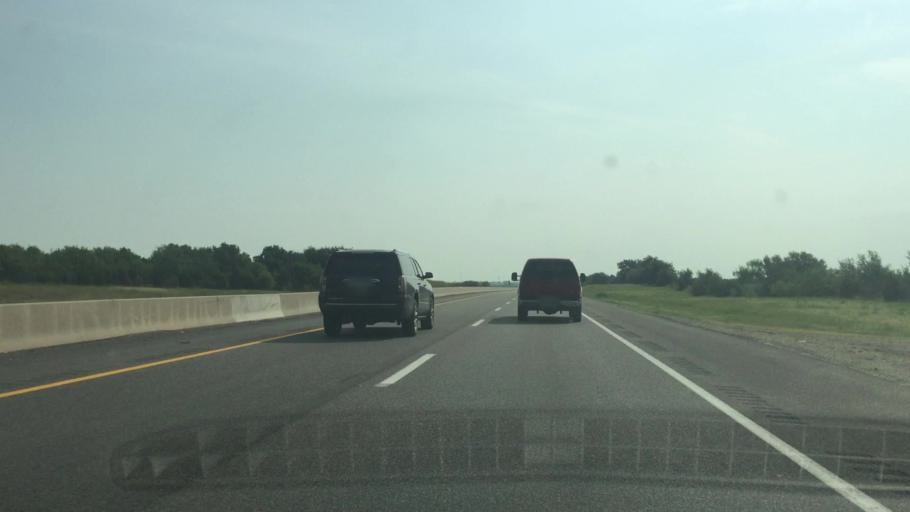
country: US
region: Kansas
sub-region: Butler County
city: Towanda
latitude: 37.7467
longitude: -97.0436
